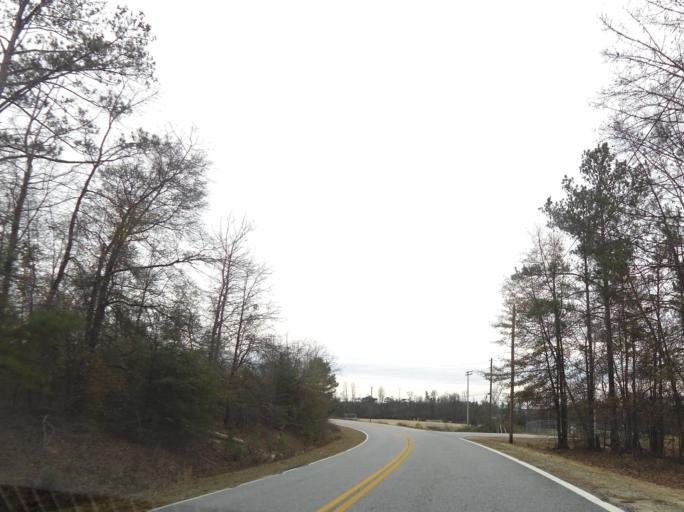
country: US
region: Georgia
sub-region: Bibb County
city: West Point
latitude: 32.8177
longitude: -83.7361
